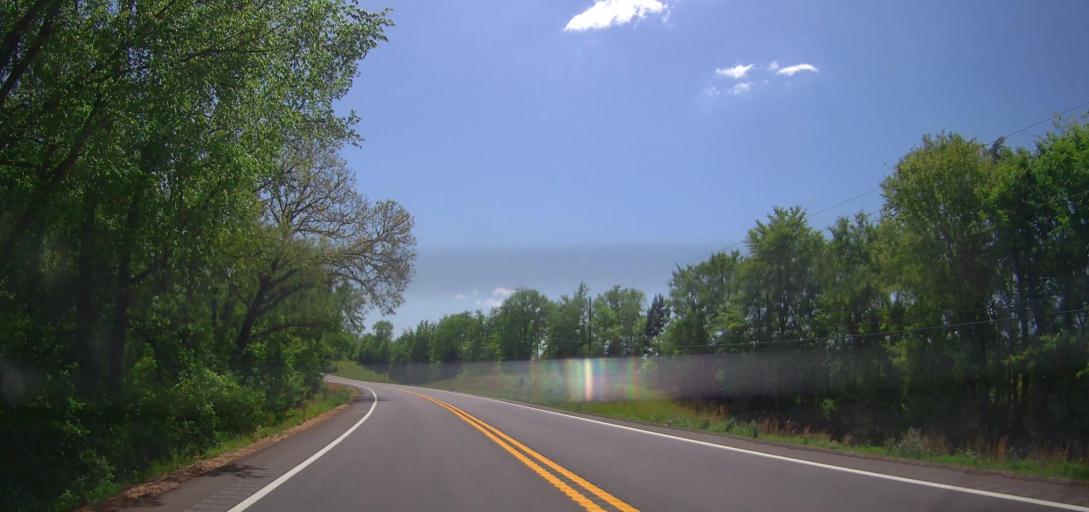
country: US
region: Georgia
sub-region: Putnam County
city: Eatonton
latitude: 33.2709
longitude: -83.4121
